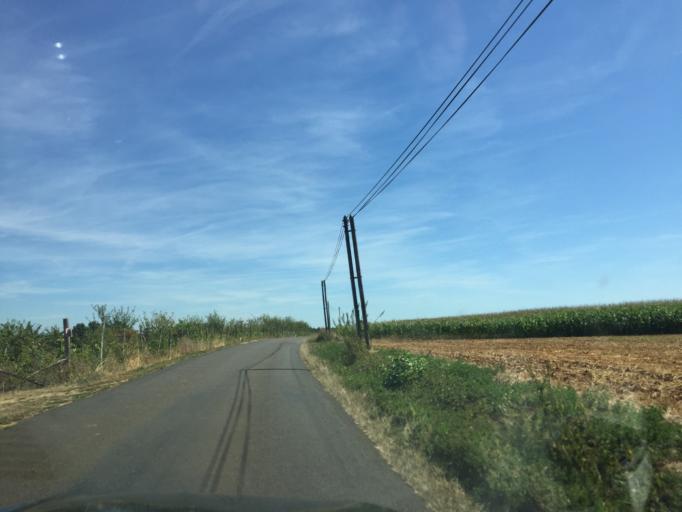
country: FR
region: Poitou-Charentes
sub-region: Departement de la Vienne
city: Iteuil
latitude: 46.4390
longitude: 0.3182
